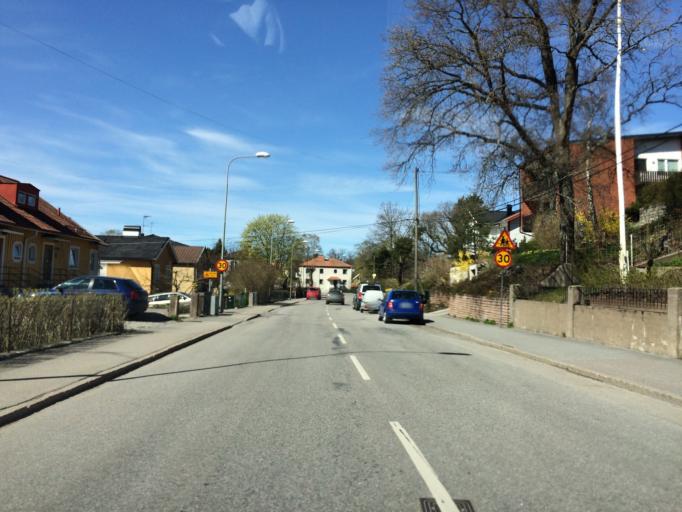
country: SE
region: Stockholm
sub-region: Huddinge Kommun
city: Segeltorp
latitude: 59.2745
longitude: 17.9626
